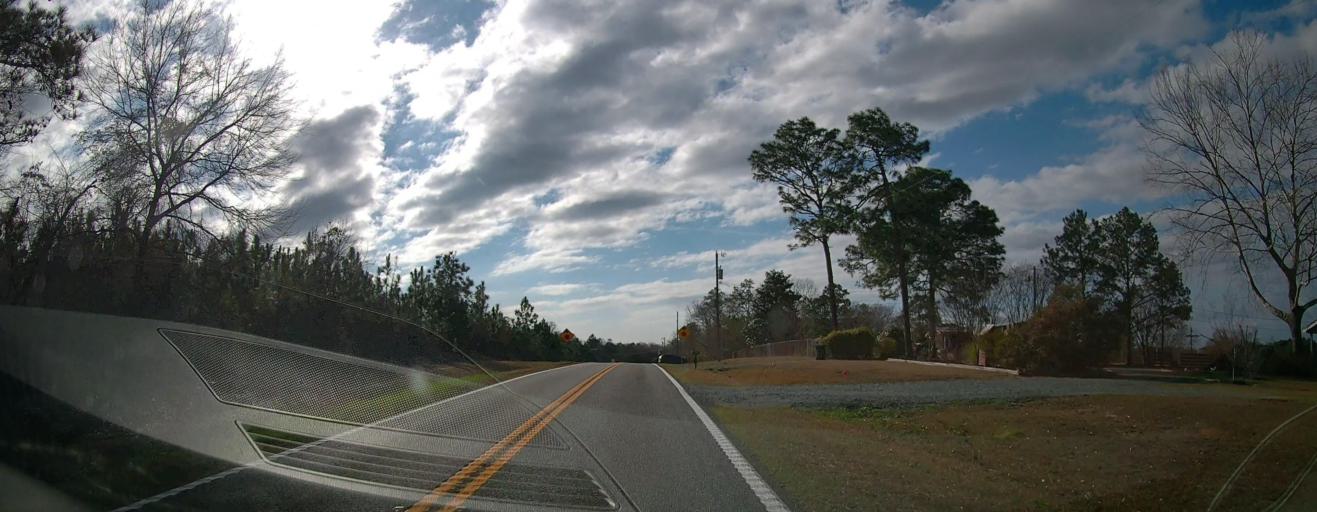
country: US
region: Georgia
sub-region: Marion County
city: Buena Vista
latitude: 32.4446
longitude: -84.5337
